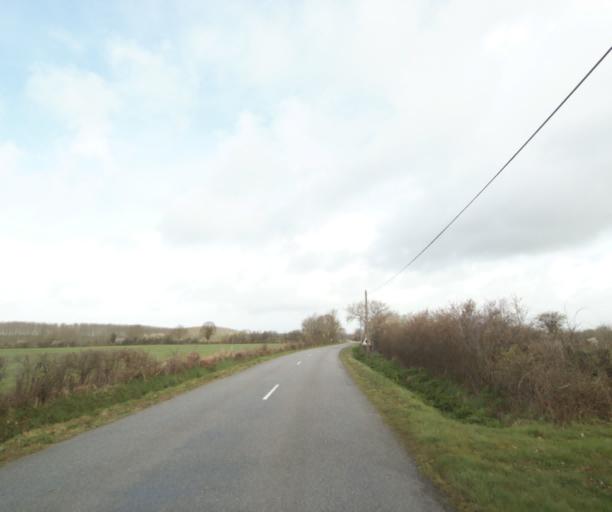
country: FR
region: Pays de la Loire
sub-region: Departement de la Loire-Atlantique
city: Bouvron
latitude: 47.4102
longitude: -1.8892
